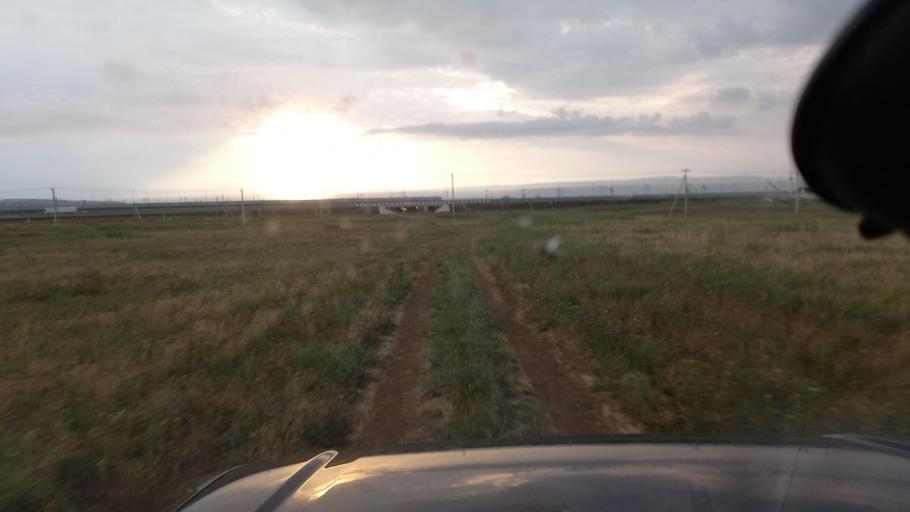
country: RU
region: Krasnodarskiy
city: Taman'
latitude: 45.2128
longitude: 36.7666
